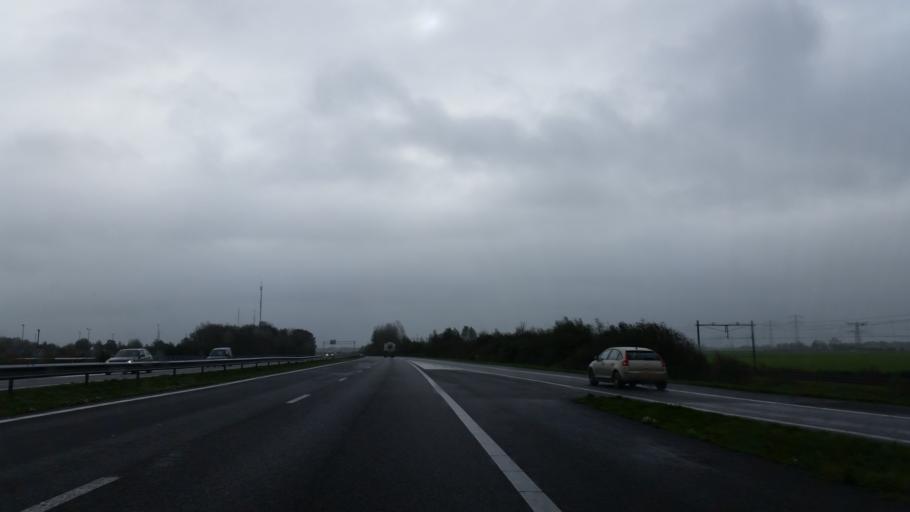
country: NL
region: Friesland
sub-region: Gemeente Boarnsterhim
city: Grou
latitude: 53.0880
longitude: 5.8243
